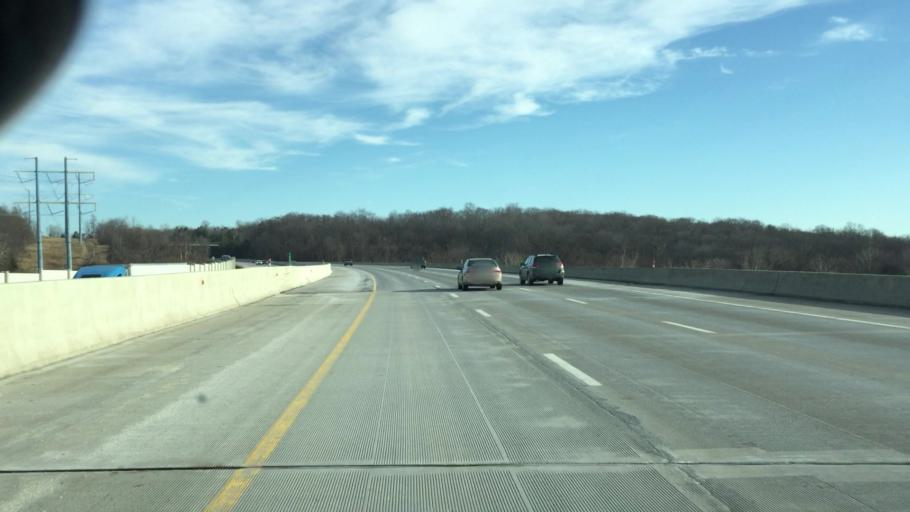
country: US
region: Ohio
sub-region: Cuyahoga County
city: North Royalton
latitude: 41.3055
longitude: -81.7445
